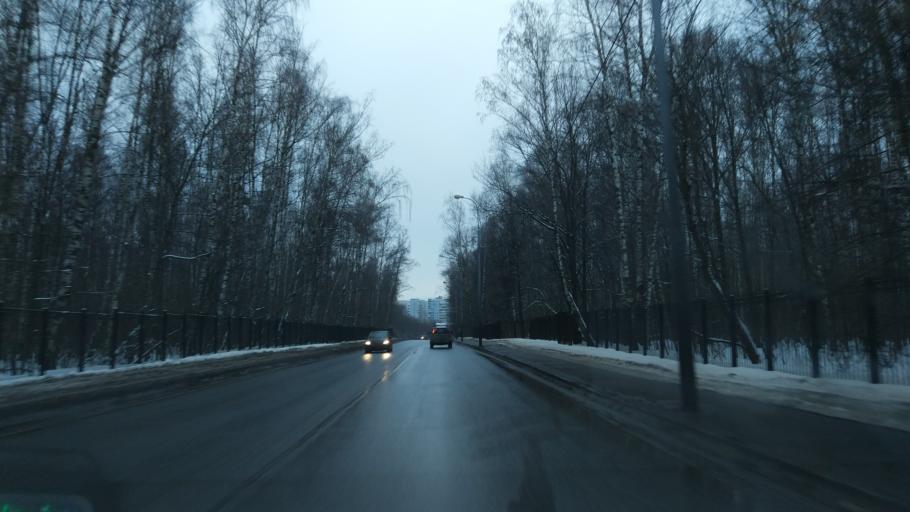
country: RU
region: Moskovskaya
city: Izmaylovo
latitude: 55.7848
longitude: 37.8201
